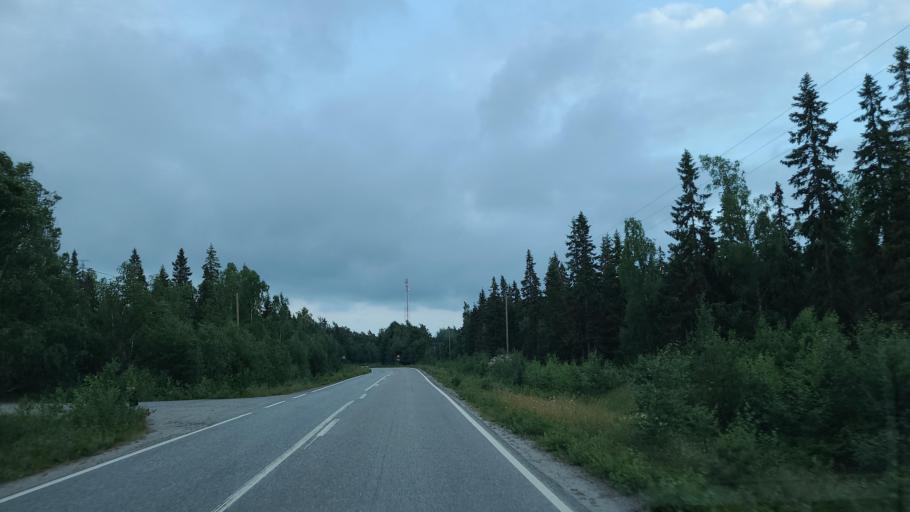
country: FI
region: Ostrobothnia
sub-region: Vaasa
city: Replot
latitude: 63.2906
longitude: 21.1112
